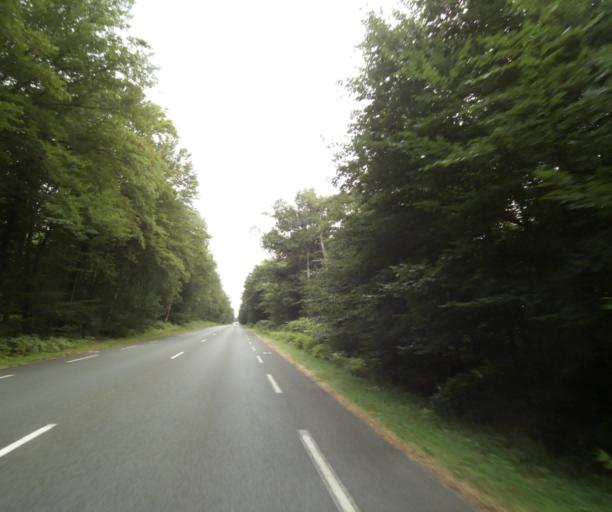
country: FR
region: Ile-de-France
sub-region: Departement de Seine-et-Marne
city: Bois-le-Roi
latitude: 48.4662
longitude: 2.6811
